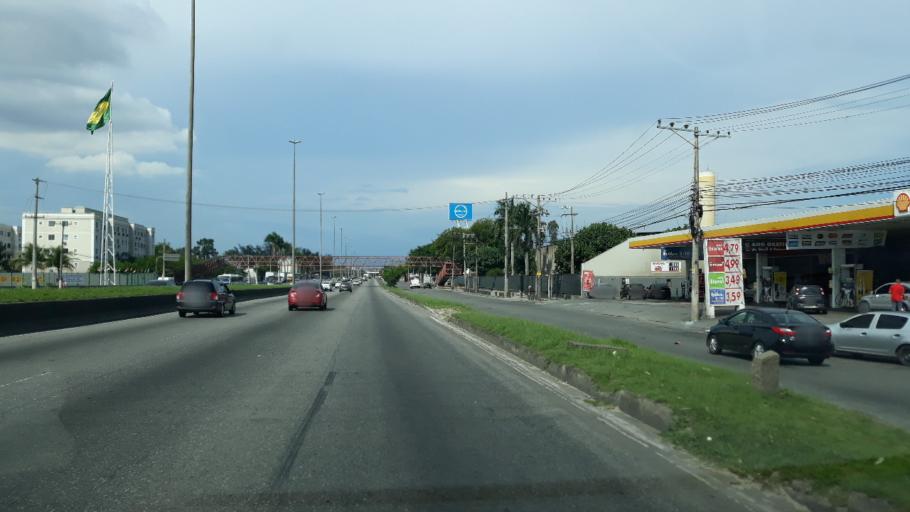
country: BR
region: Rio de Janeiro
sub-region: Sao Joao De Meriti
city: Sao Joao de Meriti
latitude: -22.8440
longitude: -43.3754
